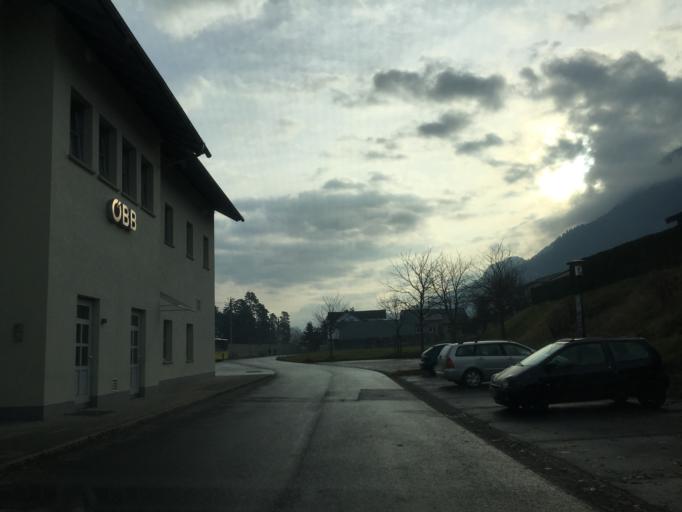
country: AT
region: Vorarlberg
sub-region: Politischer Bezirk Bludenz
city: Nenzing
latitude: 47.1910
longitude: 9.7089
